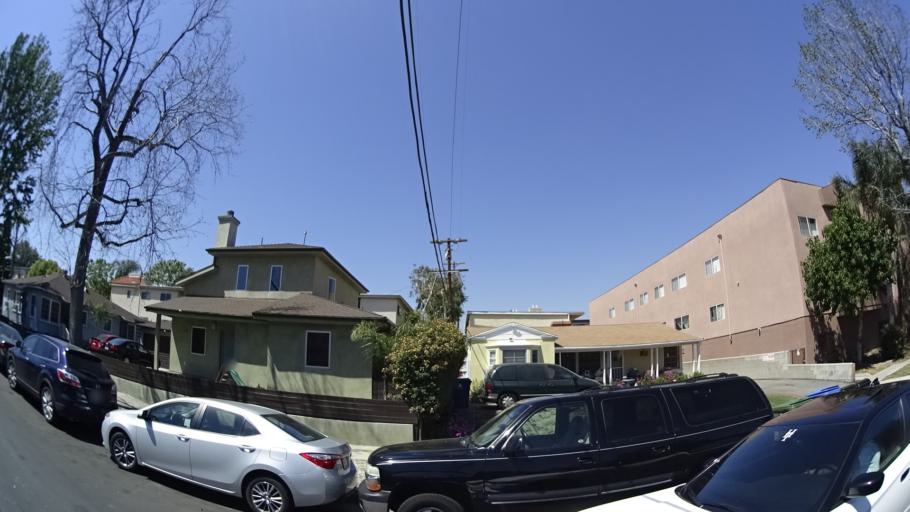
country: US
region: California
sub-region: Los Angeles County
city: North Hollywood
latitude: 34.1739
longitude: -118.3818
